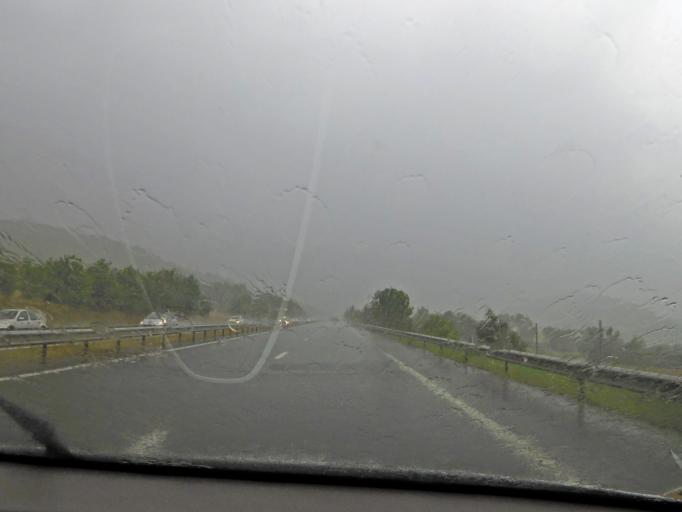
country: FR
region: Auvergne
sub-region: Departement du Cantal
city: Massiac
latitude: 45.2590
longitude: 3.2023
